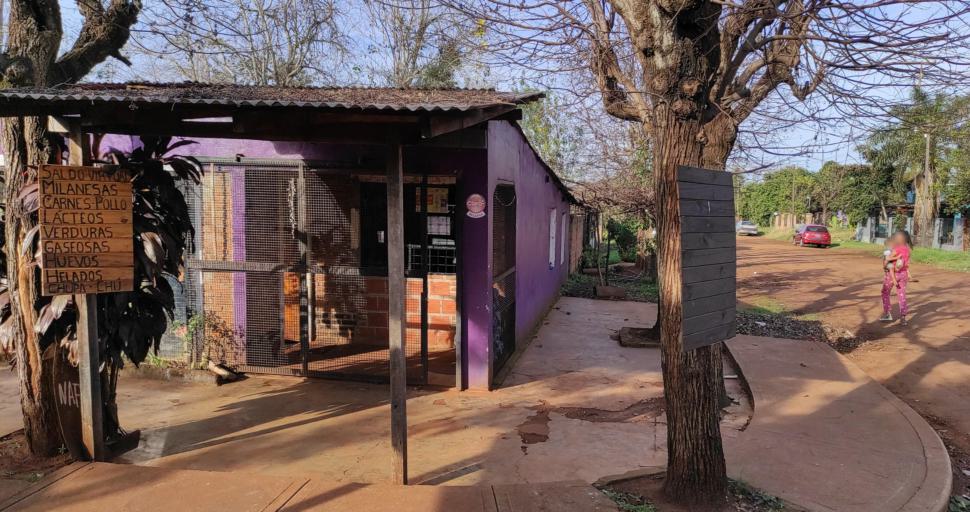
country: AR
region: Misiones
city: Garupa
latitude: -27.4851
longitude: -55.8212
